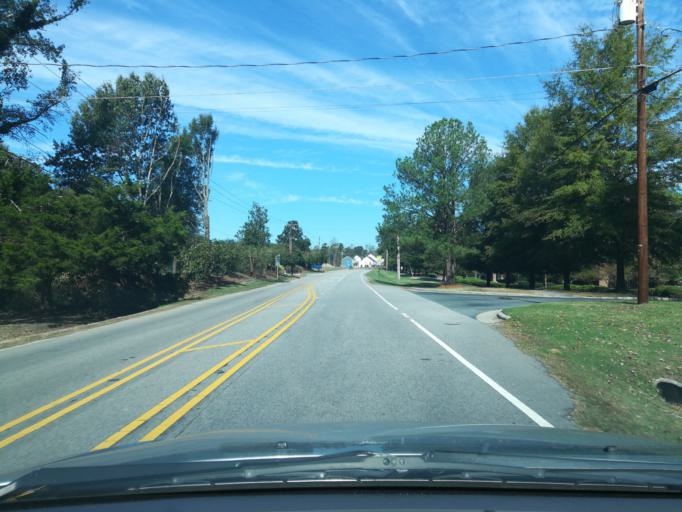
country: US
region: North Carolina
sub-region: Durham County
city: Durham
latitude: 35.9688
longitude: -78.9768
